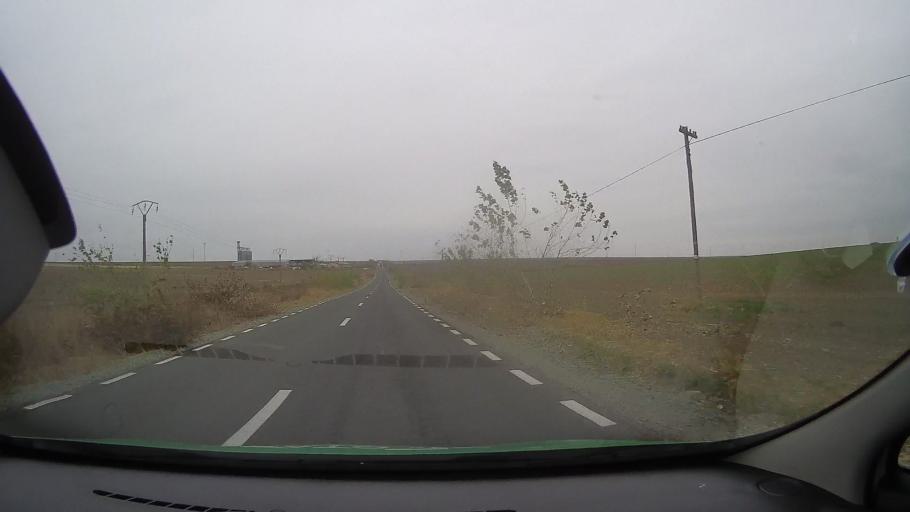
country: RO
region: Constanta
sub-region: Comuna Tortoman
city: Tortoman
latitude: 44.3601
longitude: 28.2104
